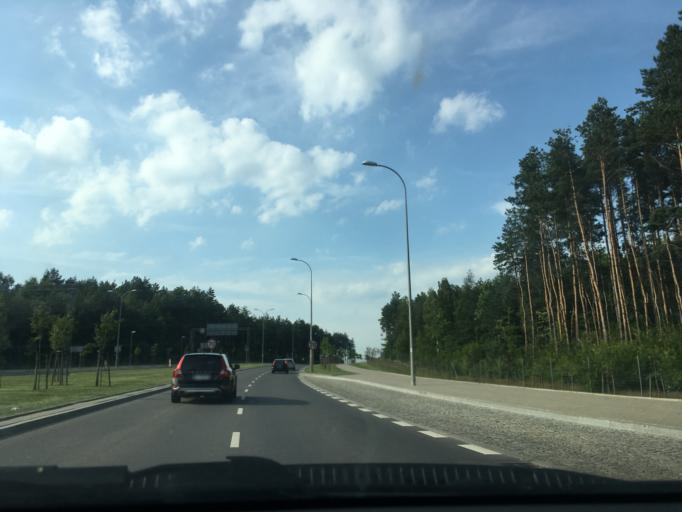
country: PL
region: Podlasie
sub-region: Bialystok
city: Bialystok
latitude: 53.1296
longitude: 23.2231
